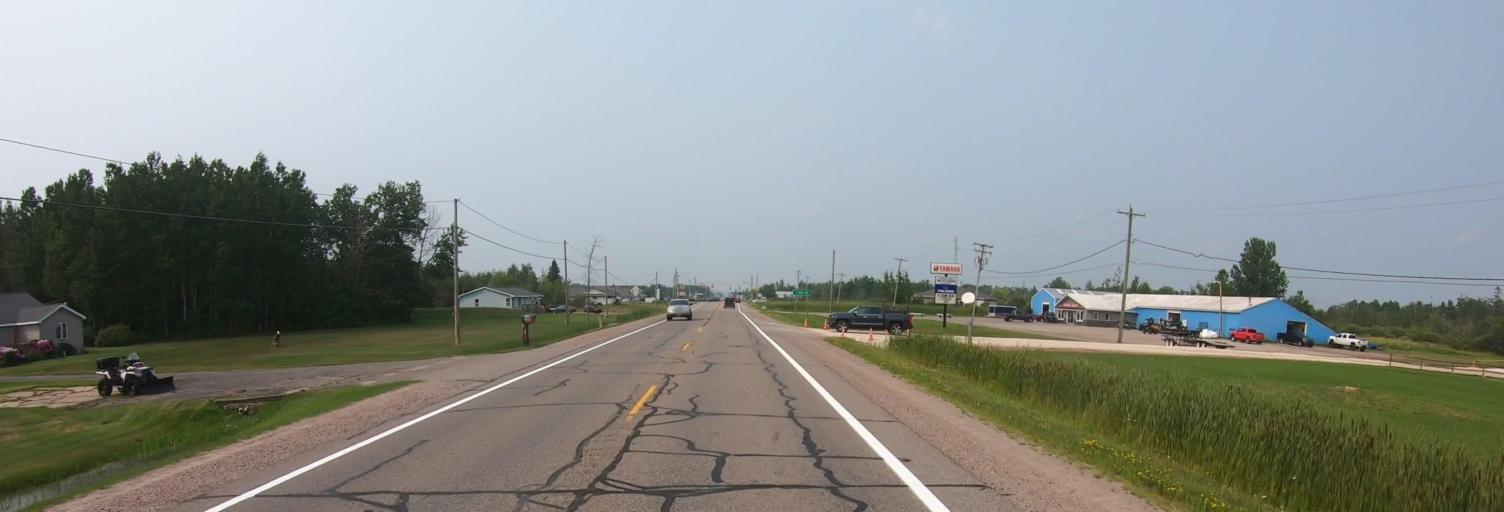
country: US
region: Michigan
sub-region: Chippewa County
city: Sault Ste. Marie
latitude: 46.4601
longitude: -84.3542
